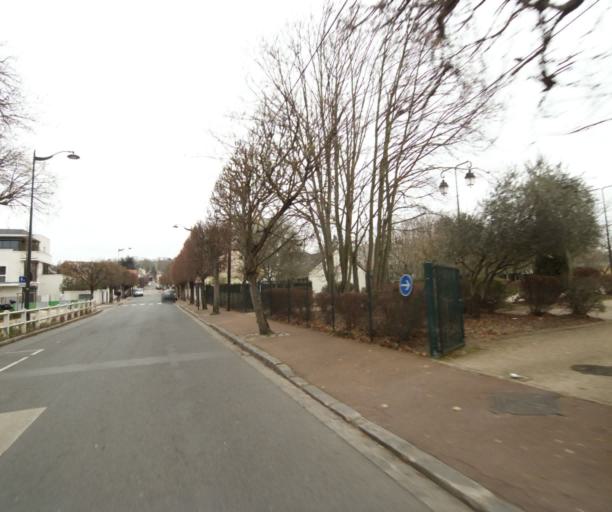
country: FR
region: Ile-de-France
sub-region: Departement des Hauts-de-Seine
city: Saint-Cloud
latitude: 48.8594
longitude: 2.1946
